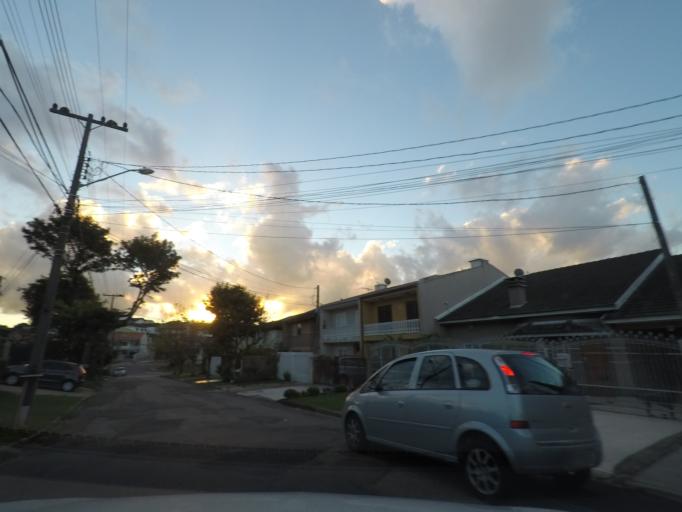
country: BR
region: Parana
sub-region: Sao Jose Dos Pinhais
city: Sao Jose dos Pinhais
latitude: -25.4997
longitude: -49.2614
